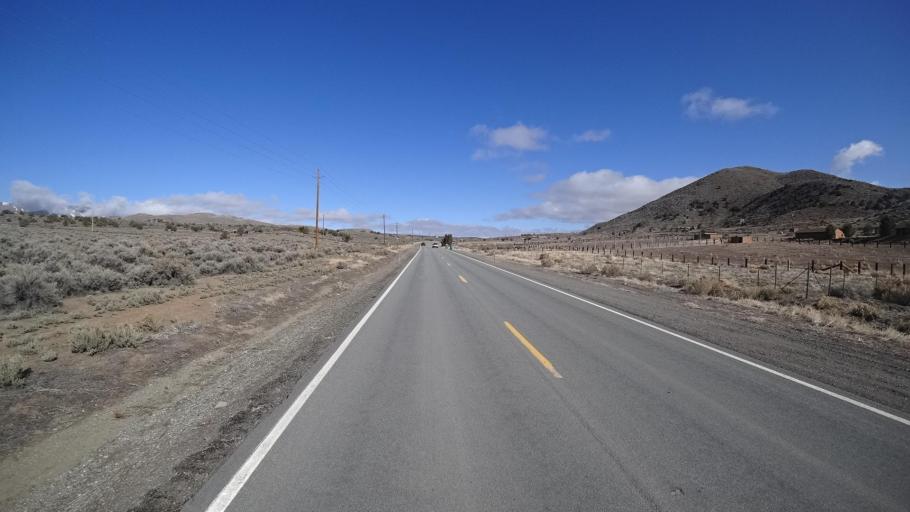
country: US
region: Nevada
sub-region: Washoe County
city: Cold Springs
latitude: 39.7418
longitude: -119.8851
